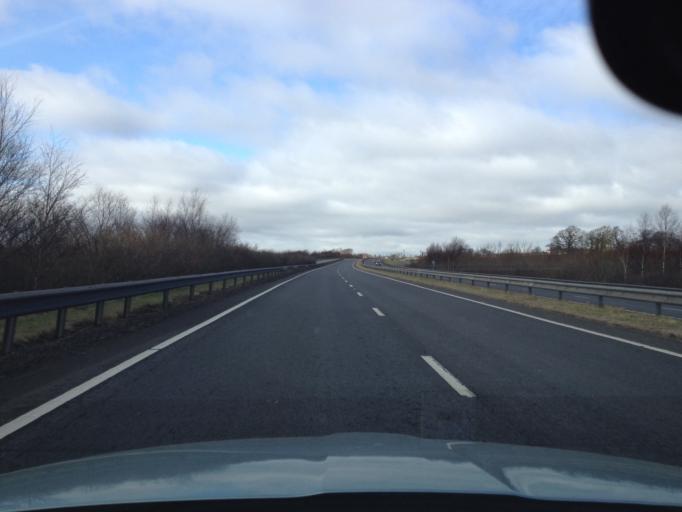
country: GB
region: Scotland
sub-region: East Lothian
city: Haddington
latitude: 55.9626
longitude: -2.7730
